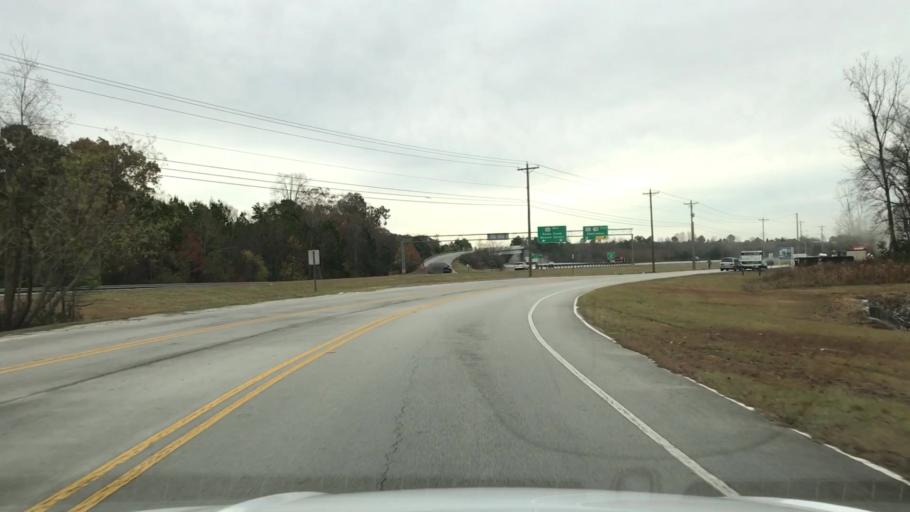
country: US
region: South Carolina
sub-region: Berkeley County
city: Goose Creek
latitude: 32.9728
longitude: -80.0541
